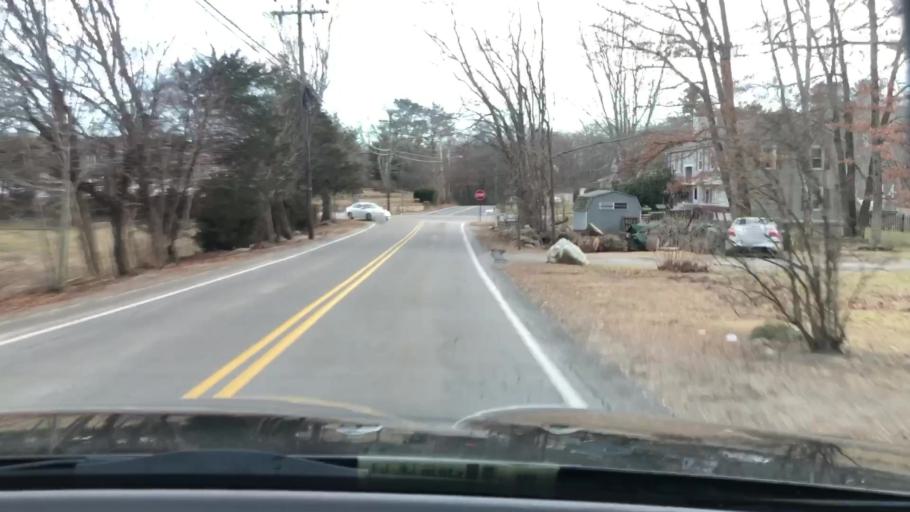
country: US
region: Massachusetts
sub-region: Worcester County
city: Blackstone
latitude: 42.0399
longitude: -71.5221
